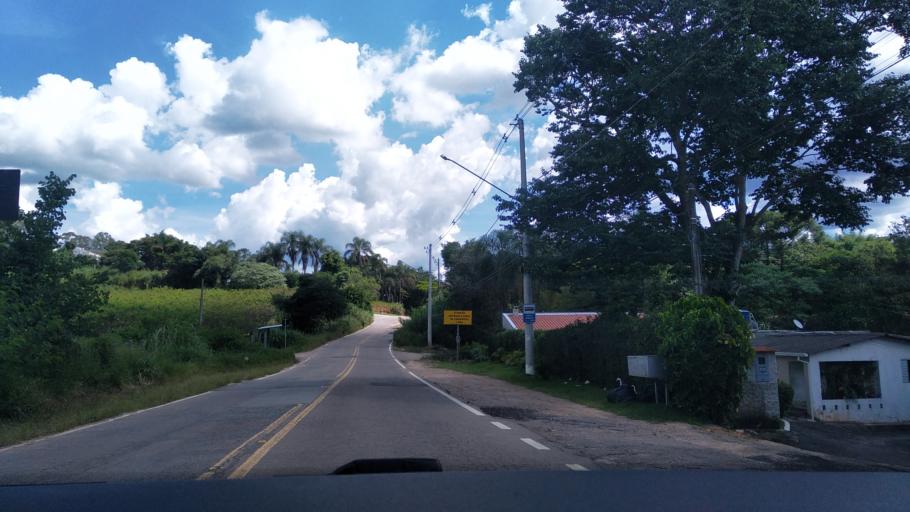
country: BR
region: Sao Paulo
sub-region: Varzea Paulista
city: Varzea Paulista
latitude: -23.2596
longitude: -46.8811
